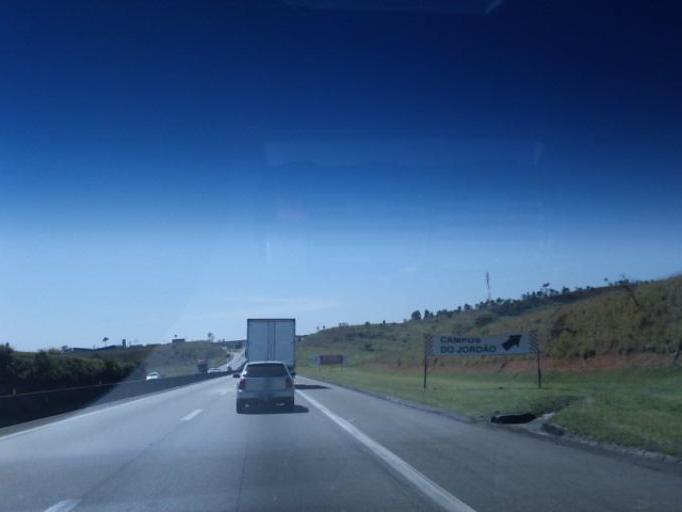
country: BR
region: Sao Paulo
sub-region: Taubate
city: Taubate
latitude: -23.0633
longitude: -45.6279
